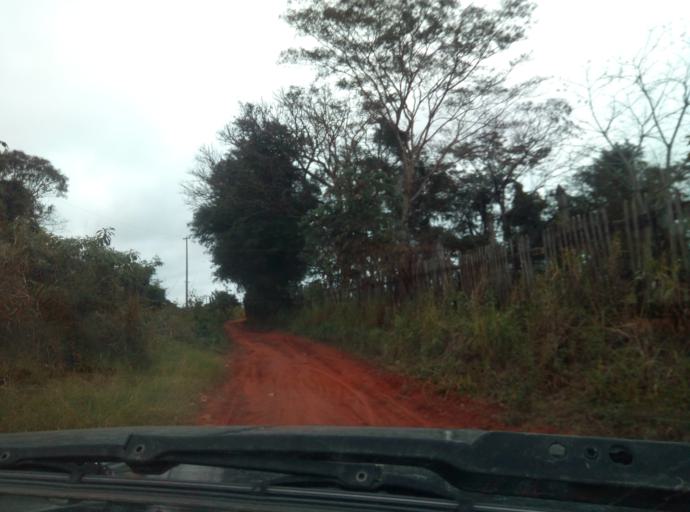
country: PY
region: Caaguazu
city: Doctor Cecilio Baez
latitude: -25.1574
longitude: -56.2716
